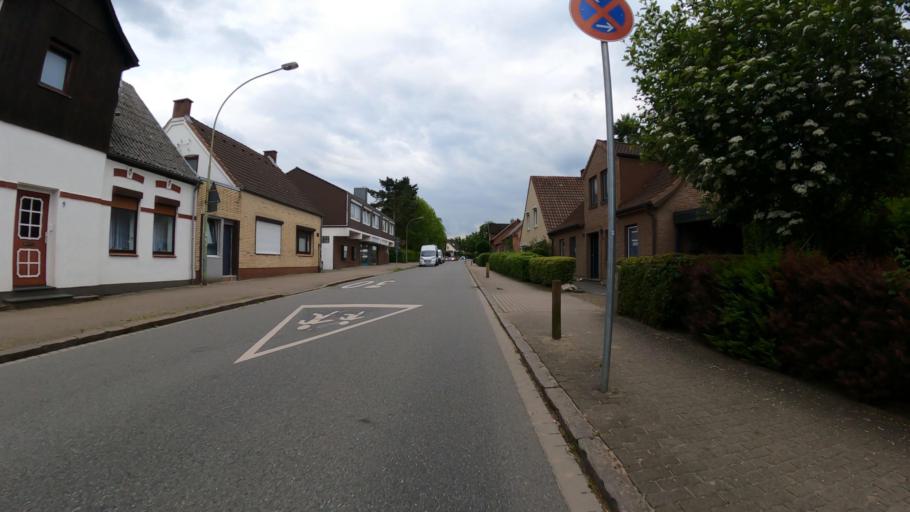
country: DE
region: Schleswig-Holstein
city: Pinneberg
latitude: 53.6574
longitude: 9.7850
